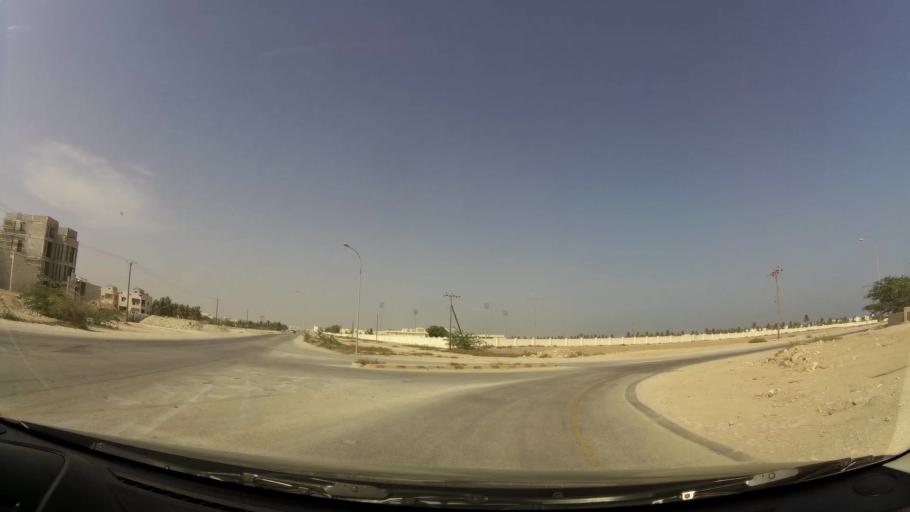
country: OM
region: Zufar
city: Salalah
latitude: 16.9913
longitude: 54.0184
